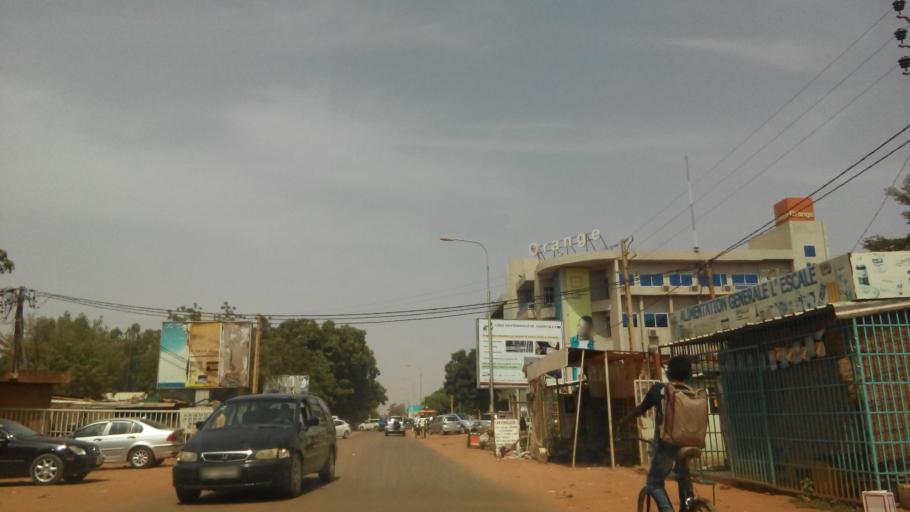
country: NE
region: Niamey
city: Niamey
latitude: 13.5294
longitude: 2.0969
